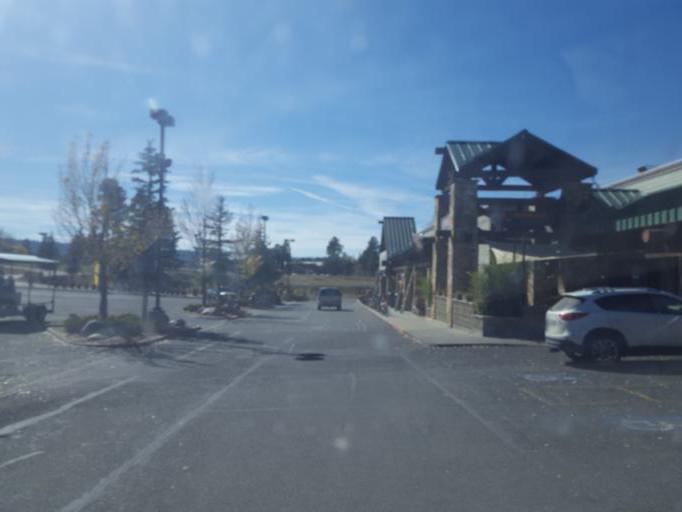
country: US
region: Colorado
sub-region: Archuleta County
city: Pagosa Springs
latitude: 37.2565
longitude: -107.0767
